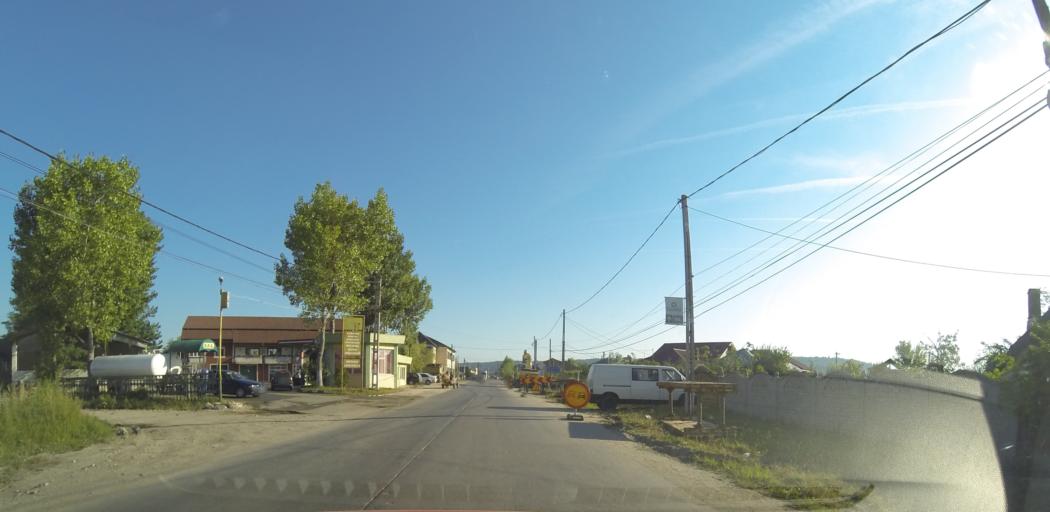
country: RO
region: Valcea
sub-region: Comuna Balcesti
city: Otetelisu
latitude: 44.6329
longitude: 23.9424
